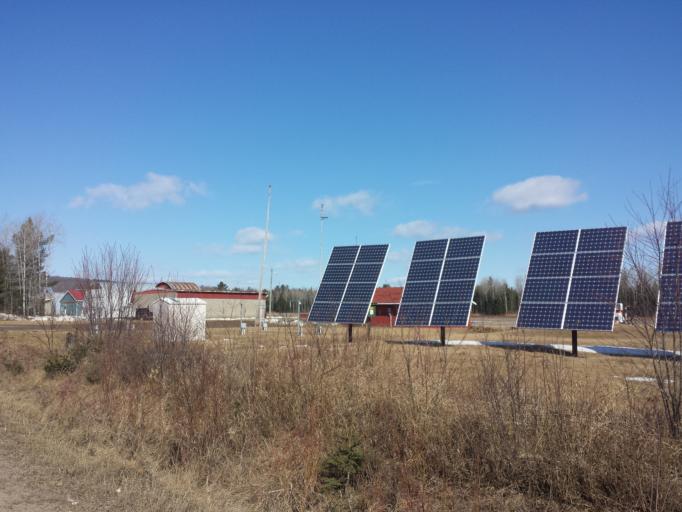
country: CA
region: Ontario
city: Bancroft
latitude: 45.0713
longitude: -77.8795
